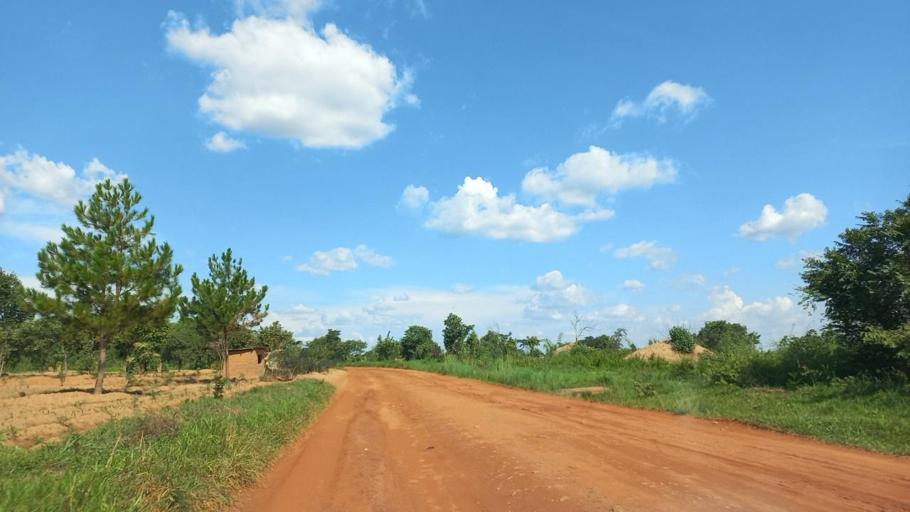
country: ZM
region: Copperbelt
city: Kitwe
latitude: -12.8700
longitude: 28.3595
